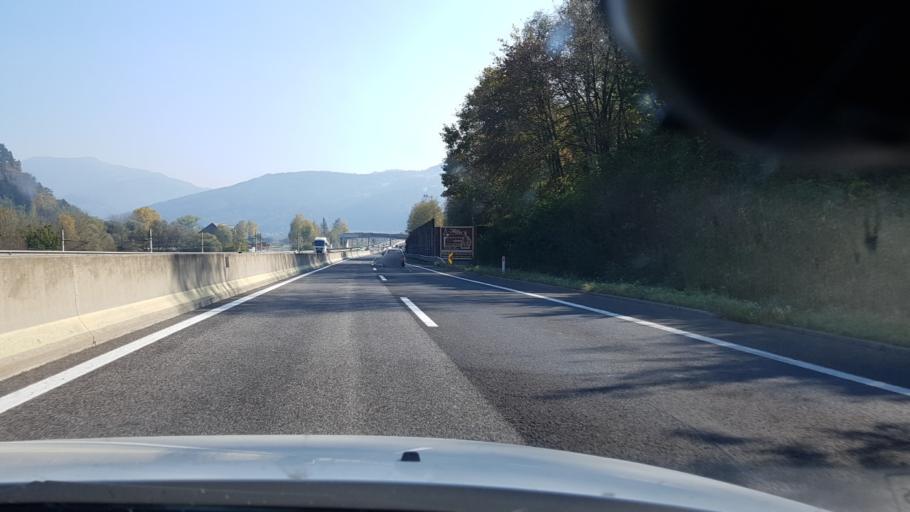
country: AT
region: Styria
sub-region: Politischer Bezirk Bruck-Muerzzuschlag
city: Oberaich
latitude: 47.4070
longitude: 15.2106
